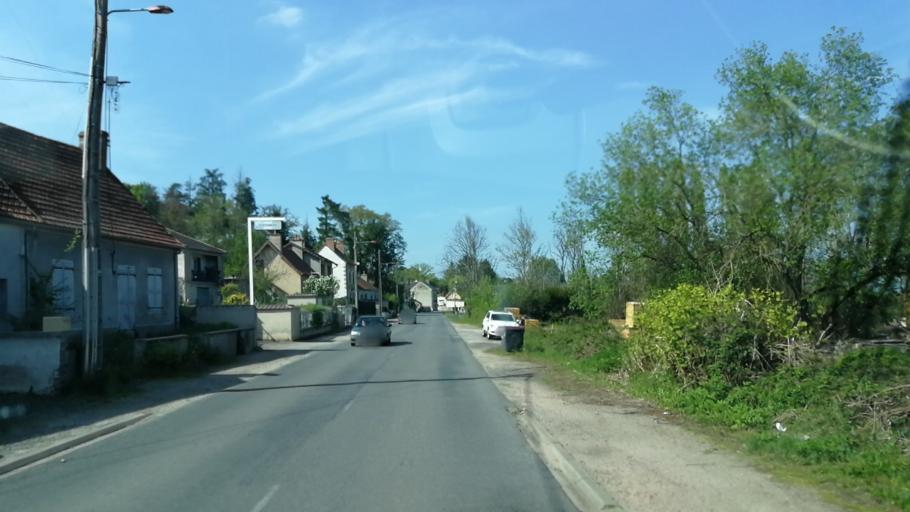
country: FR
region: Auvergne
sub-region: Departement de l'Allier
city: Saint-Gerand-le-Puy
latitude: 46.3805
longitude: 3.5831
